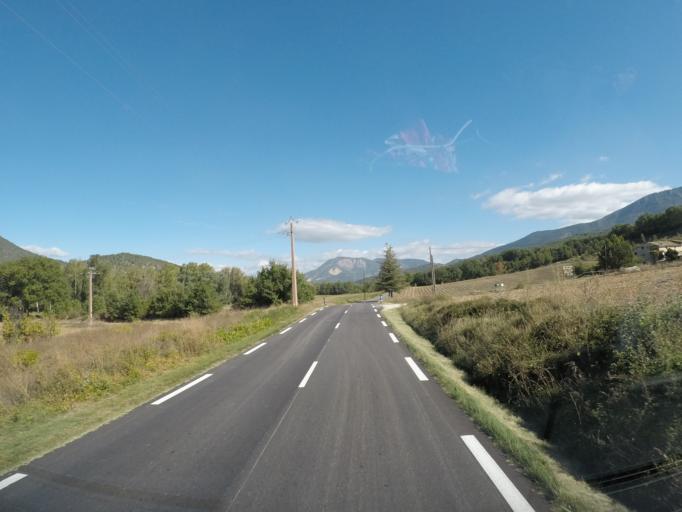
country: FR
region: Provence-Alpes-Cote d'Azur
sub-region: Departement des Alpes-de-Haute-Provence
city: Mallemoisson
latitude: 43.9551
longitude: 6.1817
